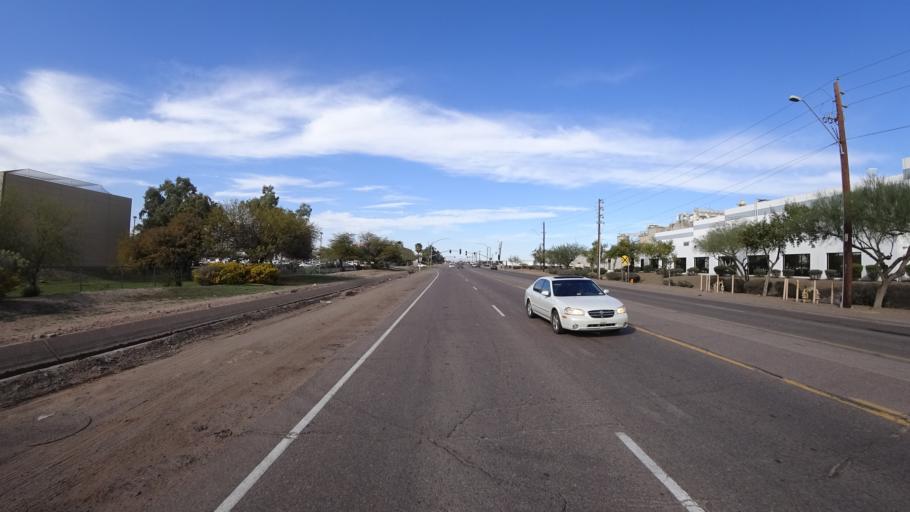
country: US
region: Arizona
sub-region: Maricopa County
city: Tolleson
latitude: 33.4404
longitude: -112.2725
